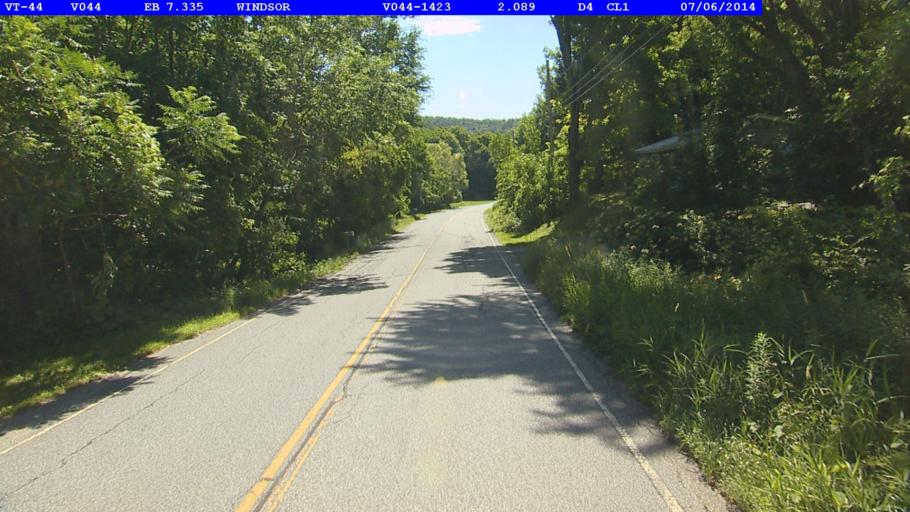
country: US
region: Vermont
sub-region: Windsor County
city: Windsor
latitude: 43.4565
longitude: -72.4154
